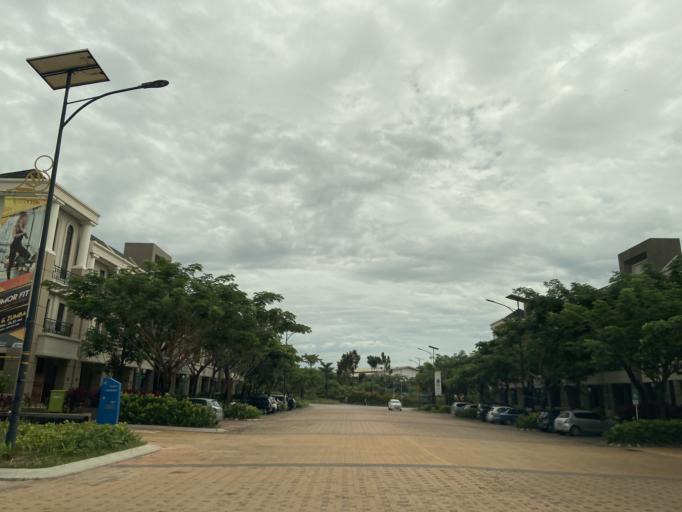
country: SG
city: Singapore
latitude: 1.1153
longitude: 104.0645
